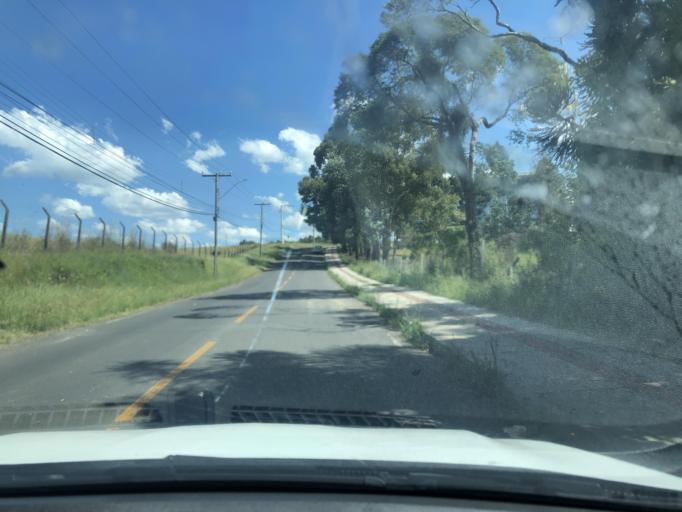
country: BR
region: Santa Catarina
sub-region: Lages
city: Lages
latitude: -27.8003
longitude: -50.3371
